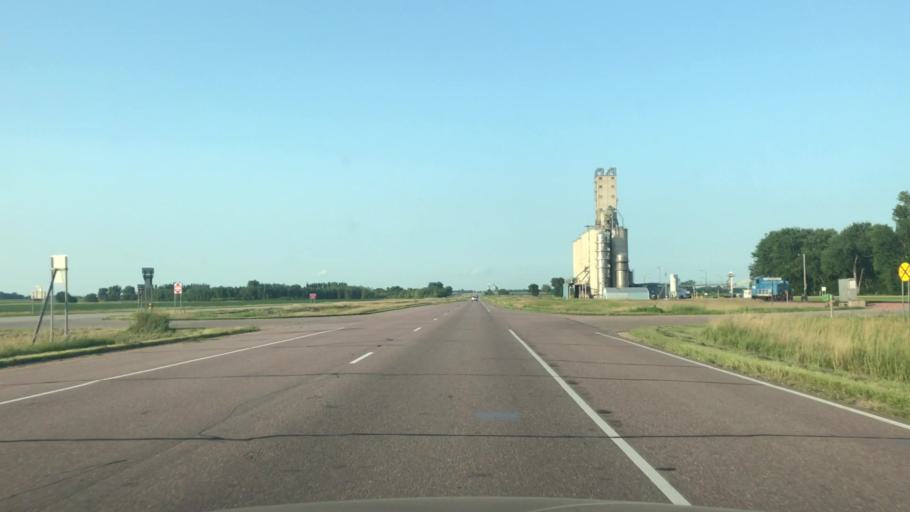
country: US
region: Minnesota
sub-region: Jackson County
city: Lakefield
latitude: 43.7657
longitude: -95.3678
